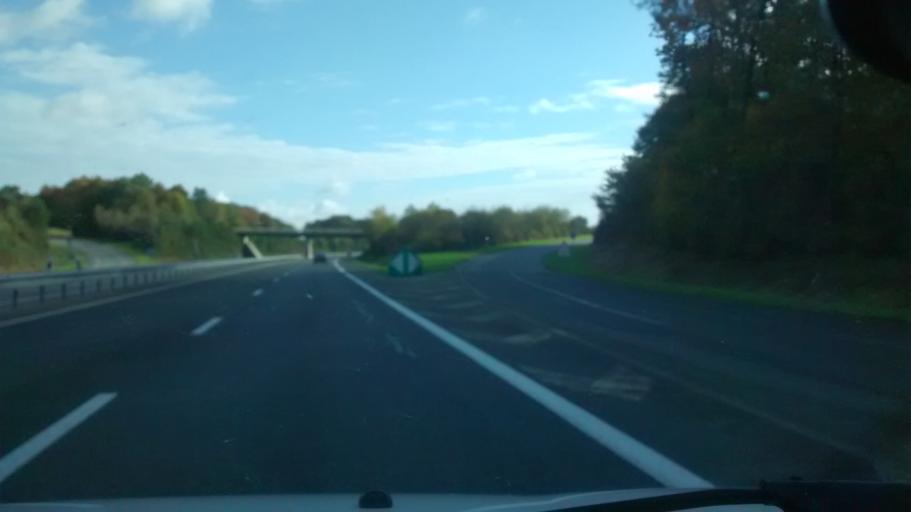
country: FR
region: Pays de la Loire
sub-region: Departement de Maine-et-Loire
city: Combree
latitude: 47.7158
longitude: -1.0146
